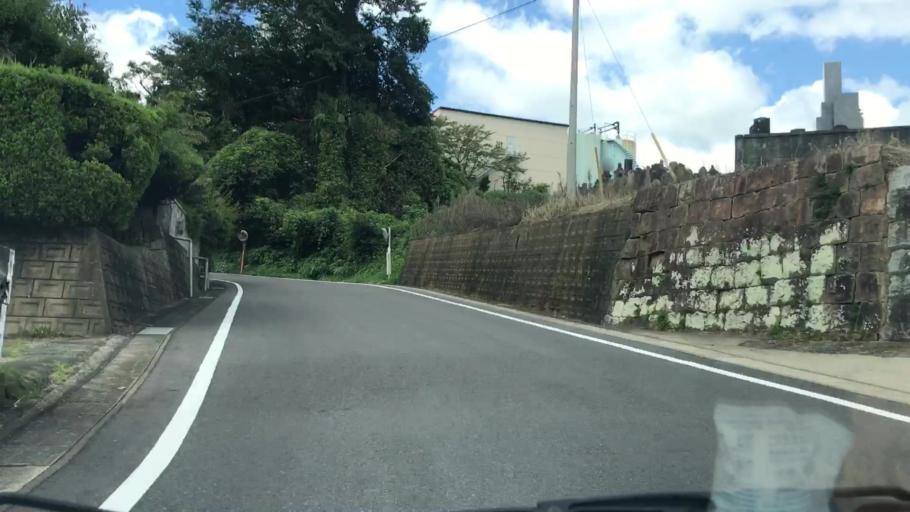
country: JP
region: Saga Prefecture
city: Takeocho-takeo
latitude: 33.2288
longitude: 130.1428
